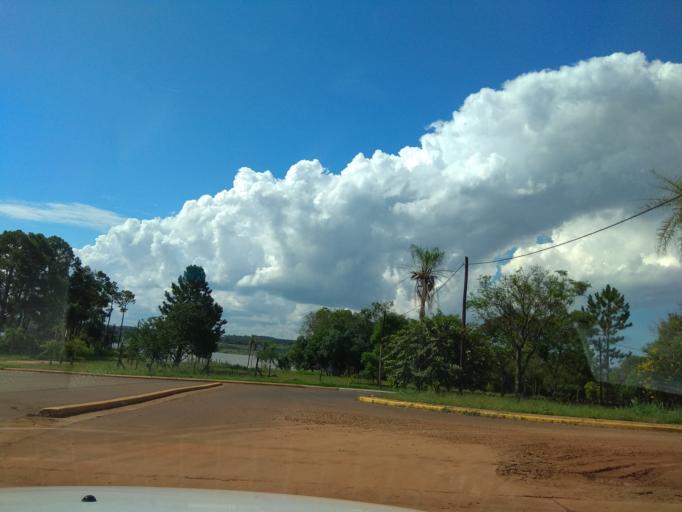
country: AR
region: Misiones
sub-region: Departamento de Candelaria
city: Candelaria
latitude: -27.4519
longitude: -55.7540
